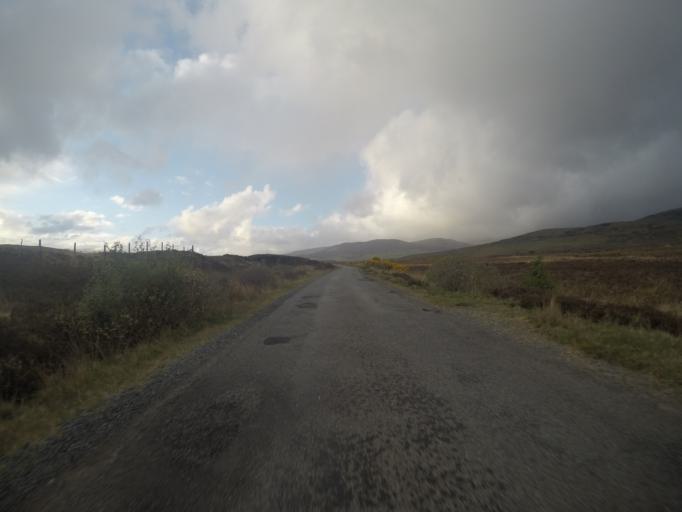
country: GB
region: Scotland
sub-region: Highland
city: Isle of Skye
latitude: 57.4601
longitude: -6.2968
